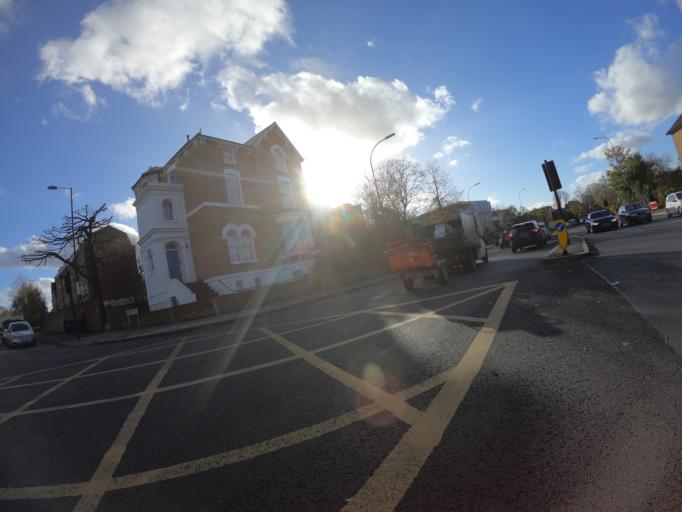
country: GB
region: England
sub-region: Greater London
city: Blackheath
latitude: 51.4463
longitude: 0.0146
